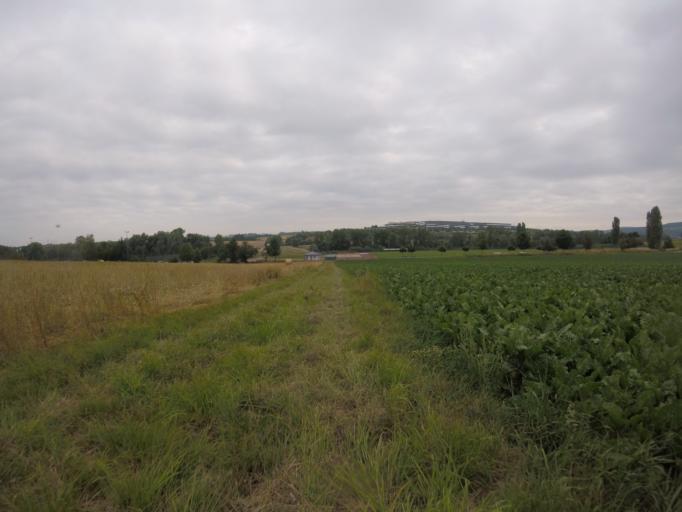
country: DE
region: Baden-Wuerttemberg
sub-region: Regierungsbezirk Stuttgart
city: Abstatt
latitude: 49.0695
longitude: 9.3036
